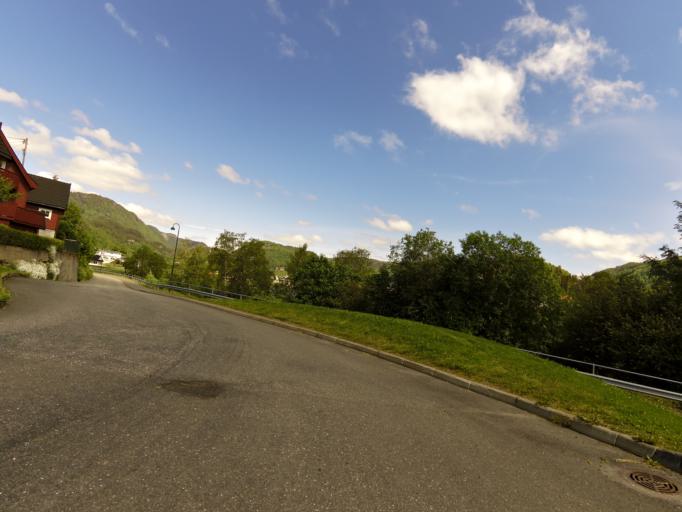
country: NO
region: Vest-Agder
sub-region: Kvinesdal
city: Liknes
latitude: 58.3116
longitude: 6.9596
